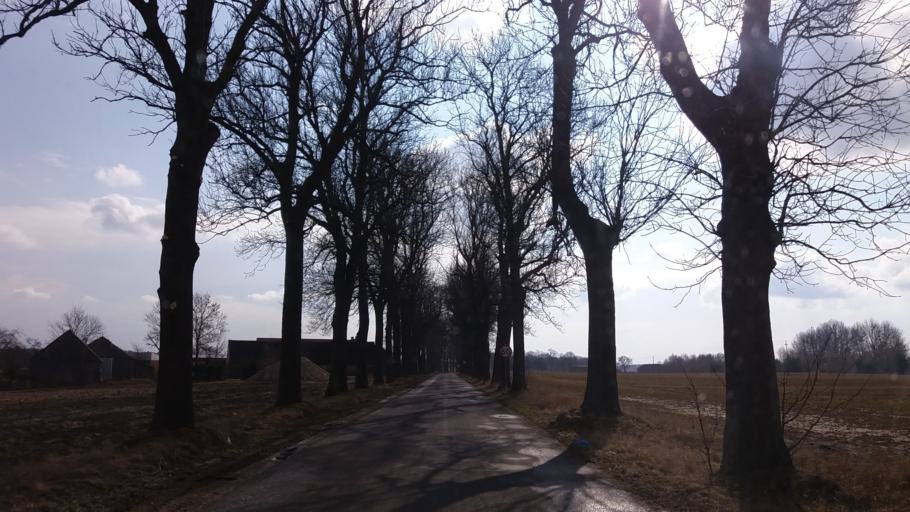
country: PL
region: West Pomeranian Voivodeship
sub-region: Powiat choszczenski
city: Recz
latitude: 53.1786
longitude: 15.6035
